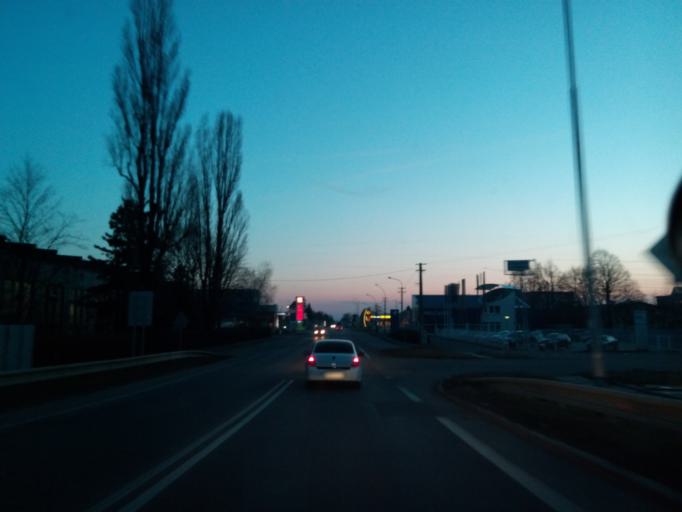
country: SK
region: Kosicky
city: Michalovce
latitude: 48.7451
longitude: 21.9000
